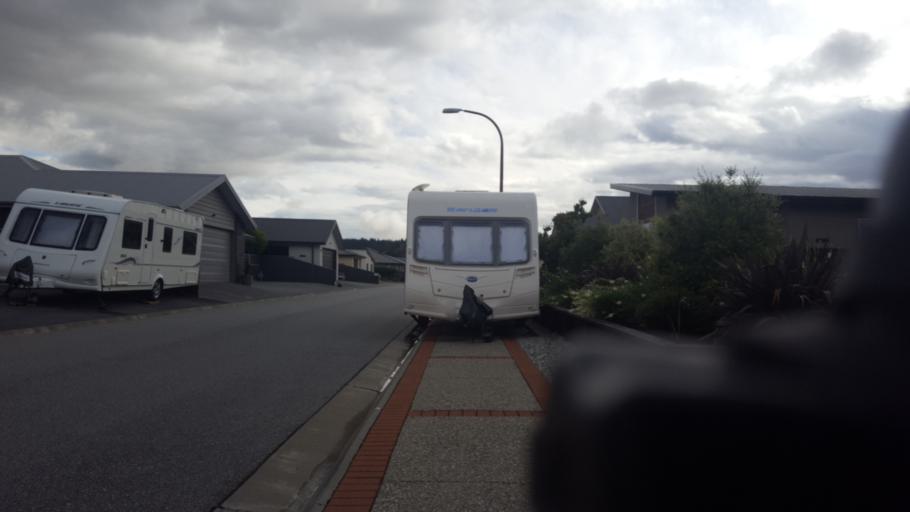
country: NZ
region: Otago
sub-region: Queenstown-Lakes District
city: Wanaka
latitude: -45.2413
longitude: 169.3788
